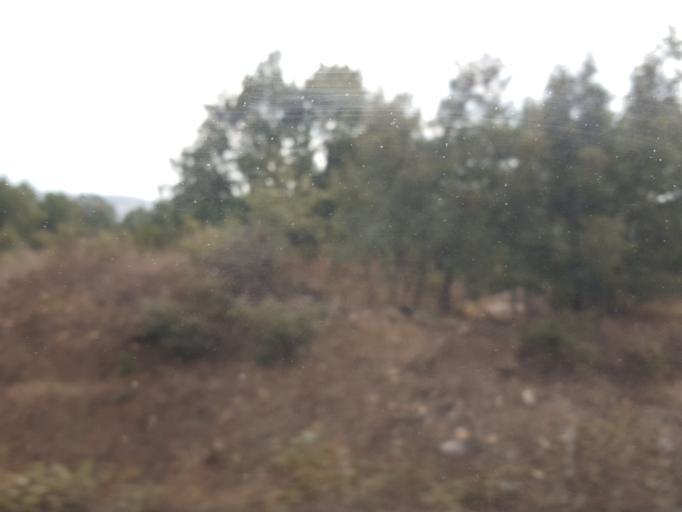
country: TR
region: Amasya
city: Gediksaray
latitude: 40.4811
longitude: 35.7778
